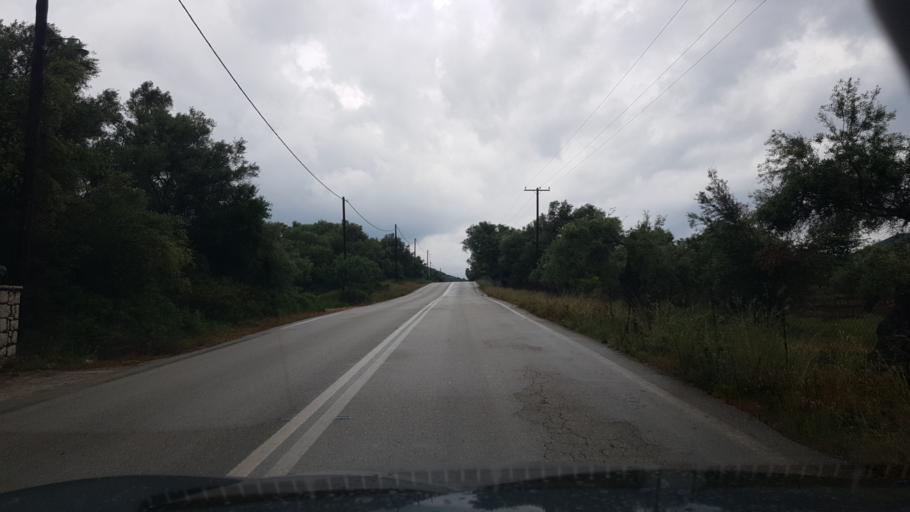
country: GR
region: Ionian Islands
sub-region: Lefkada
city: Nidri
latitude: 38.6362
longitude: 20.6723
